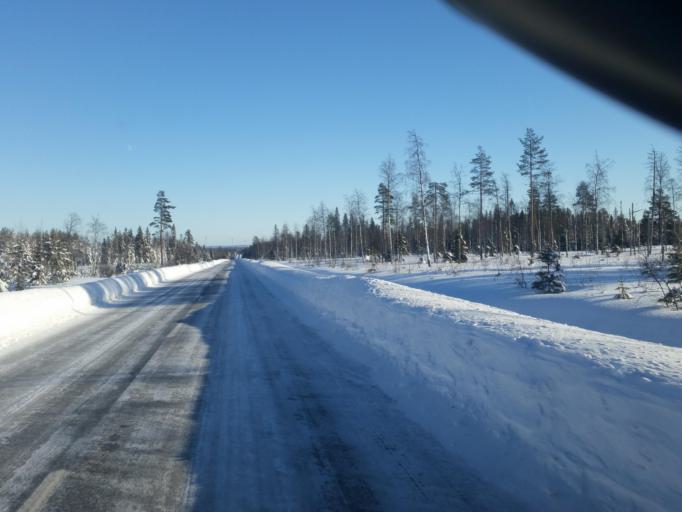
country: SE
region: Vaesterbotten
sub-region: Skelleftea Kommun
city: Storvik
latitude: 65.3240
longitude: 20.7809
